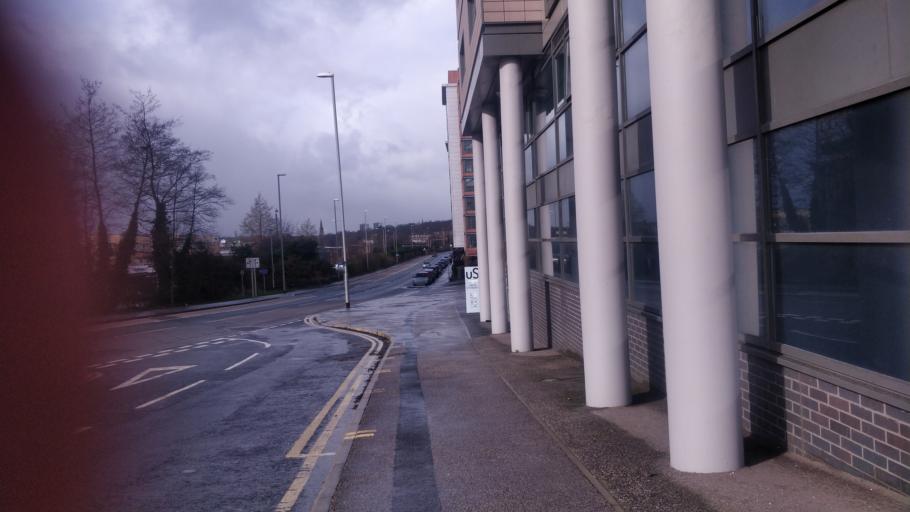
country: GB
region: England
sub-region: City and Borough of Leeds
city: Leeds
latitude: 53.8014
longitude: -1.5632
